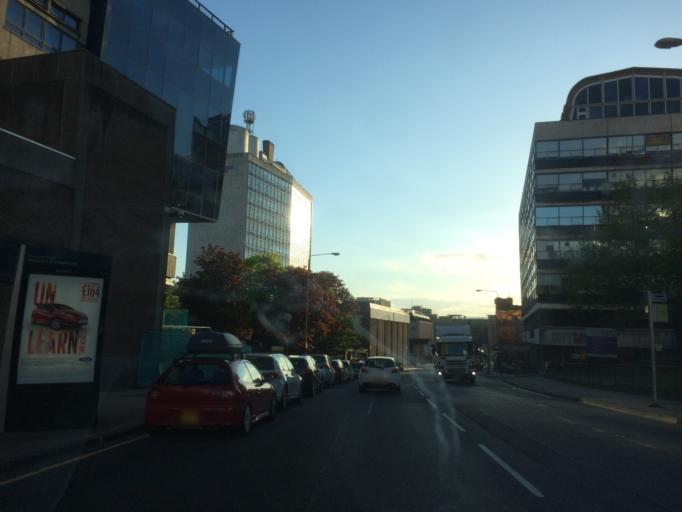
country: GB
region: Scotland
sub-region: Glasgow City
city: Glasgow
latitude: 55.8630
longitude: -4.2460
